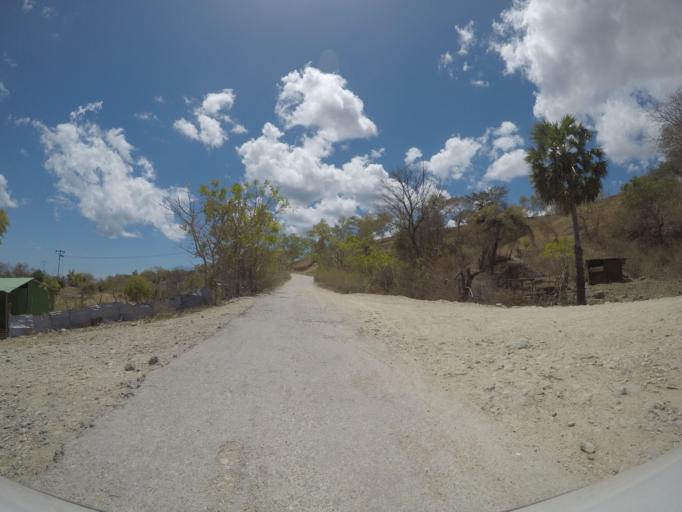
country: TL
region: Baucau
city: Baucau
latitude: -8.4841
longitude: 126.6107
